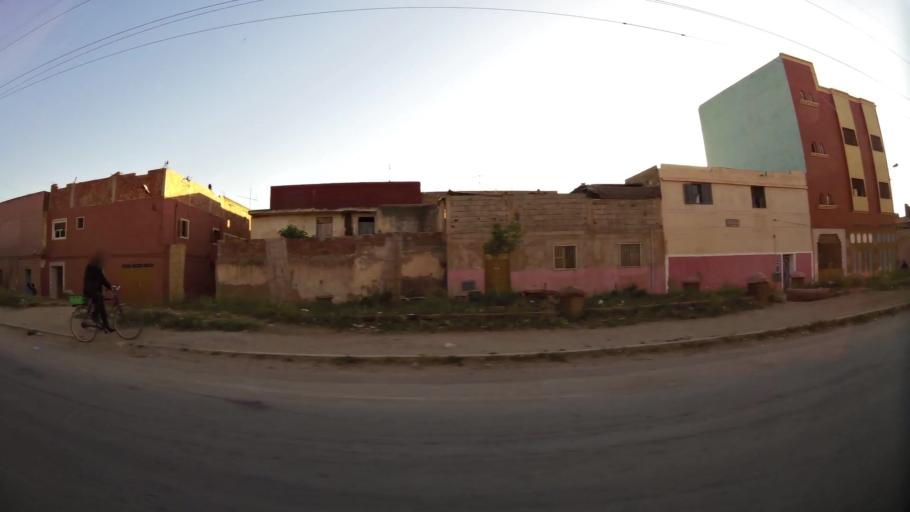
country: MA
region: Oriental
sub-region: Berkane-Taourirt
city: Berkane
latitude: 34.9226
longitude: -2.3122
